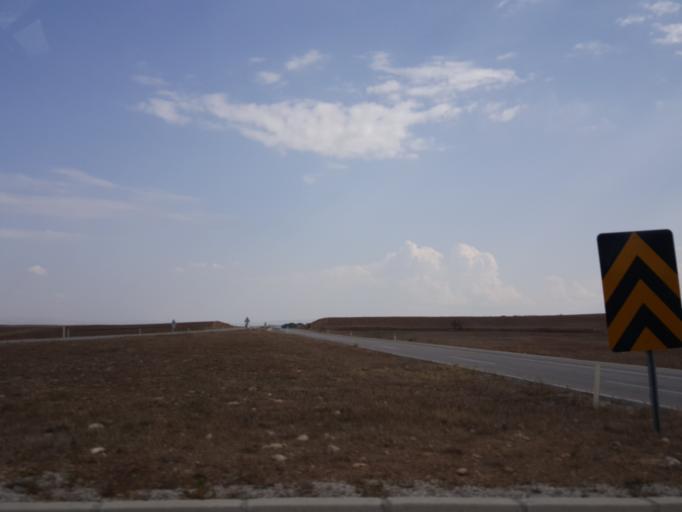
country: TR
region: Corum
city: Alaca
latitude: 40.1381
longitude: 34.7892
